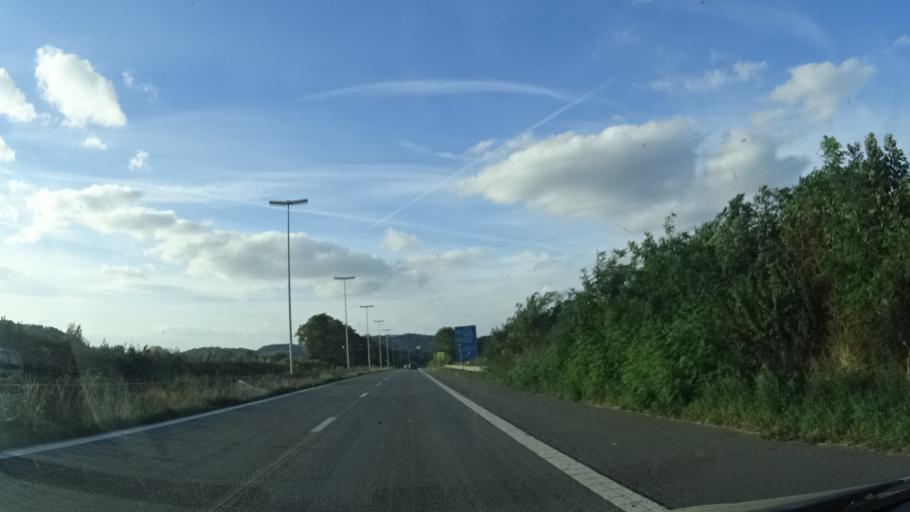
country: BE
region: Wallonia
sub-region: Province du Hainaut
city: Frameries
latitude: 50.4199
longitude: 3.9178
